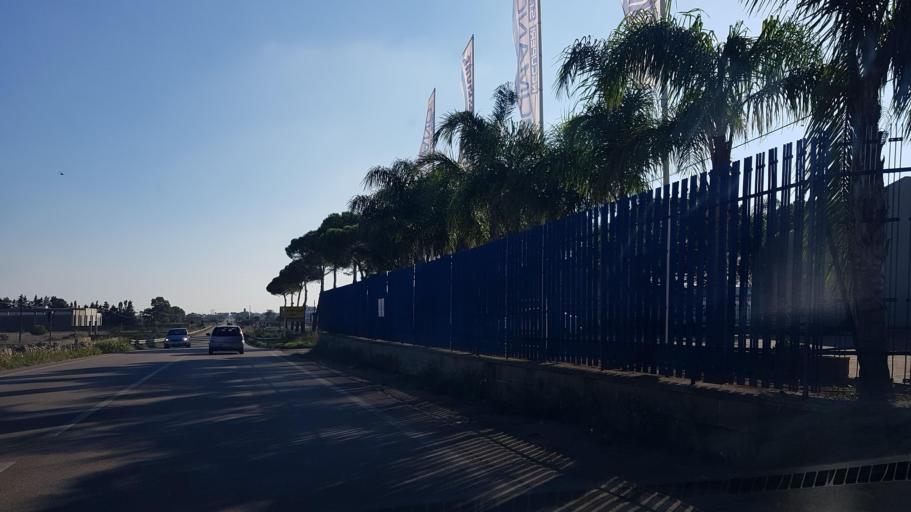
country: IT
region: Apulia
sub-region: Provincia di Lecce
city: Montesano Salentino
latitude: 40.0042
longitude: 18.3237
